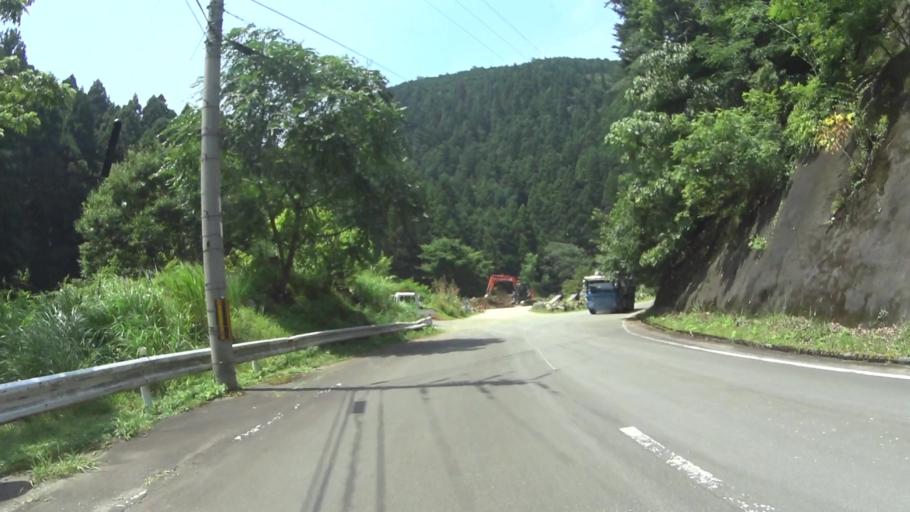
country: JP
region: Kyoto
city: Maizuru
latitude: 35.3196
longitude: 135.4457
